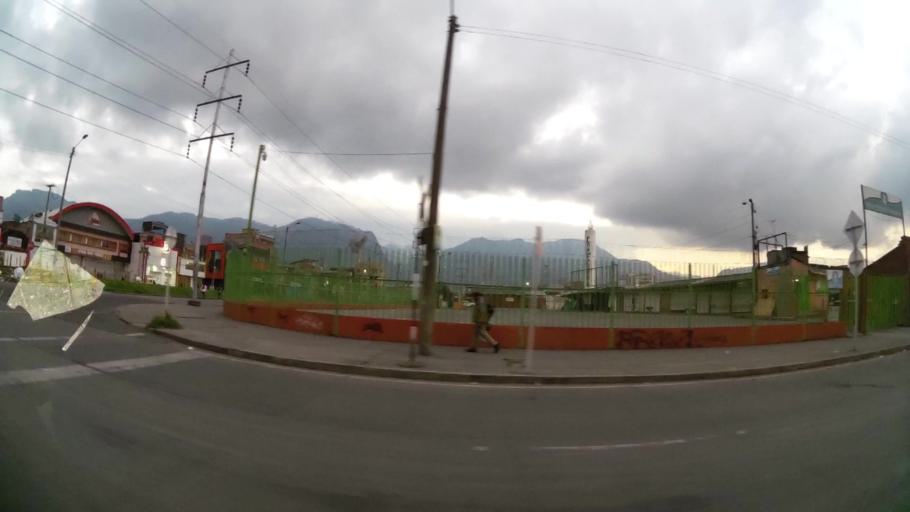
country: CO
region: Bogota D.C.
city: Bogota
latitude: 4.6178
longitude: -74.0844
